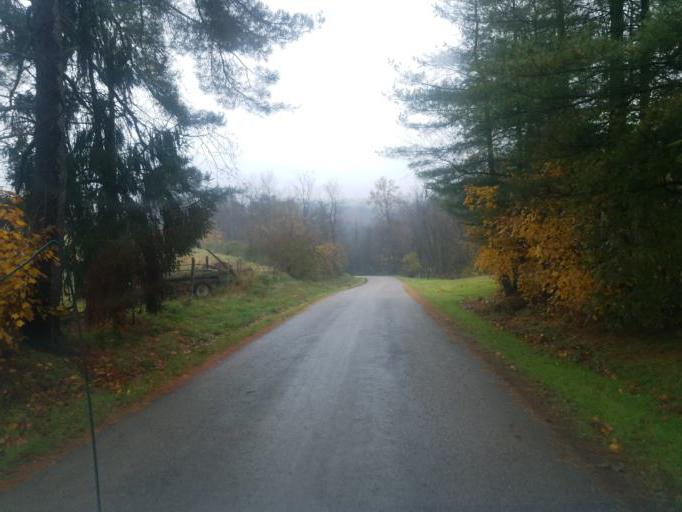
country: US
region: Ohio
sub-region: Morgan County
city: McConnelsville
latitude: 39.4980
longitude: -81.8061
